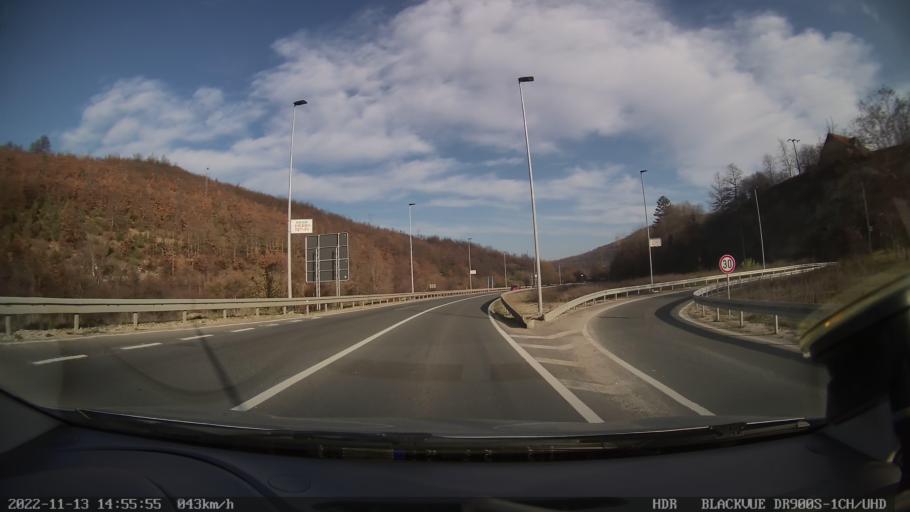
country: RS
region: Central Serbia
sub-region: Zlatiborski Okrug
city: Cajetina
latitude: 43.7842
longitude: 19.7395
